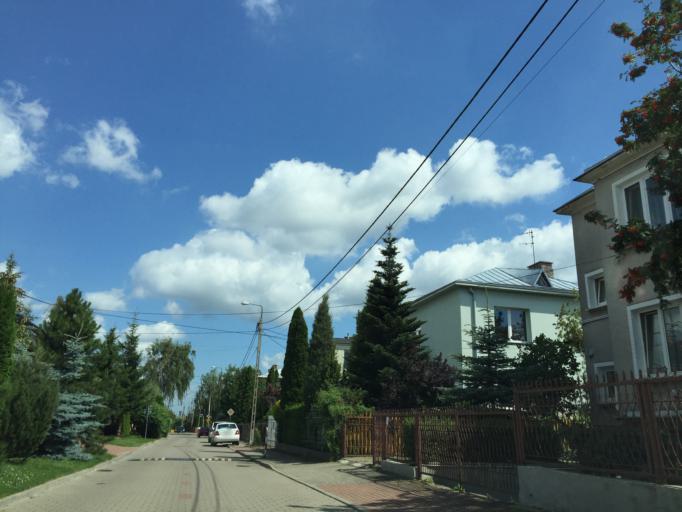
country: PL
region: Podlasie
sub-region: Bialystok
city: Bialystok
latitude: 53.1154
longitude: 23.1725
